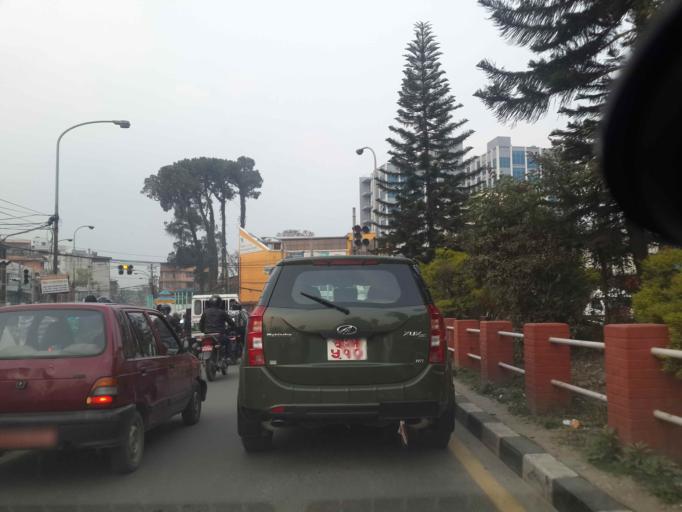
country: NP
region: Central Region
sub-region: Bagmati Zone
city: Kathmandu
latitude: 27.6902
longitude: 85.3174
